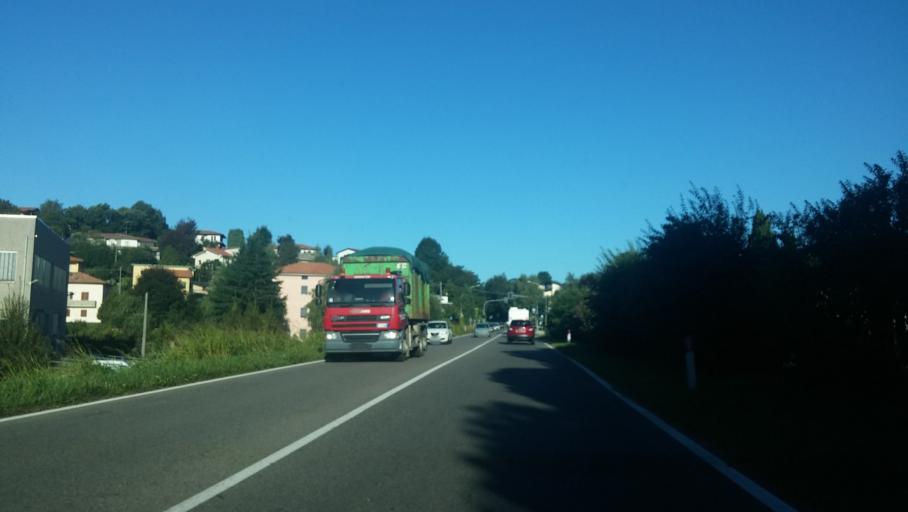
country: IT
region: Lombardy
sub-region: Provincia di Como
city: Albese Con Cassano
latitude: 45.7940
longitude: 9.1649
